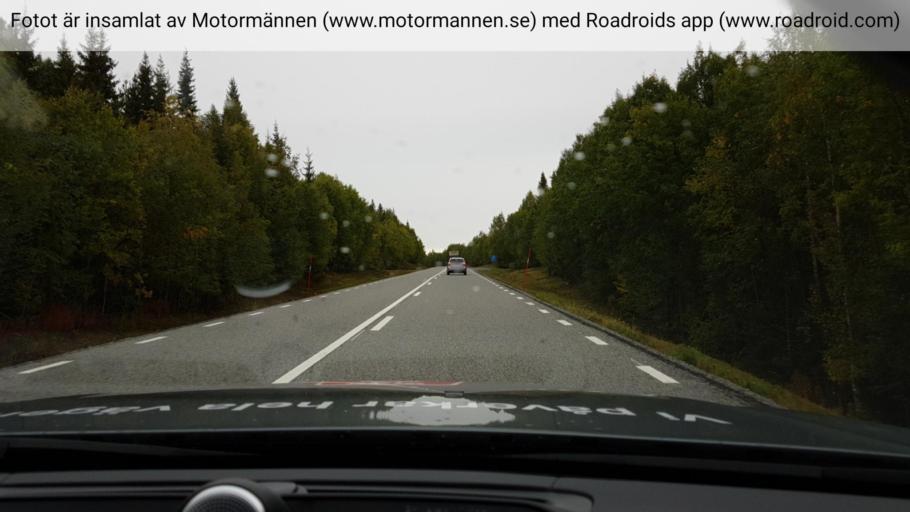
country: SE
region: Jaemtland
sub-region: Stroemsunds Kommun
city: Stroemsund
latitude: 64.0811
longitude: 15.5627
